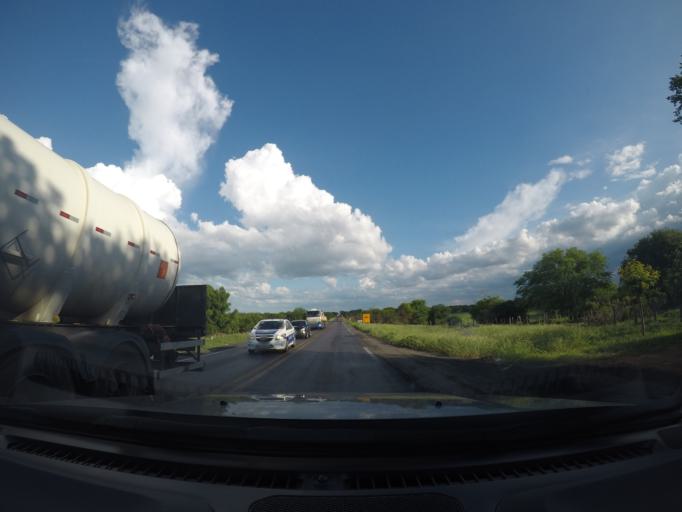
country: BR
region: Bahia
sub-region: Oliveira Dos Brejinhos
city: Oliveira dos Brejinhos
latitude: -12.1005
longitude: -42.9195
